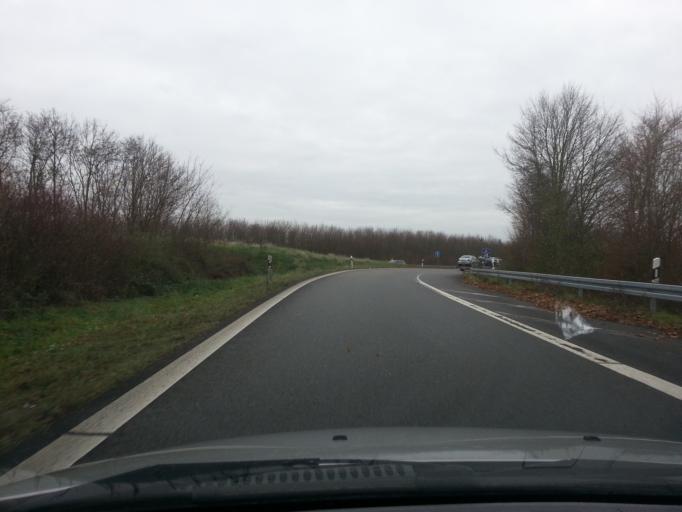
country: DE
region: Baden-Wuerttemberg
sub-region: Karlsruhe Region
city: Ketsch
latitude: 49.3572
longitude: 8.5465
